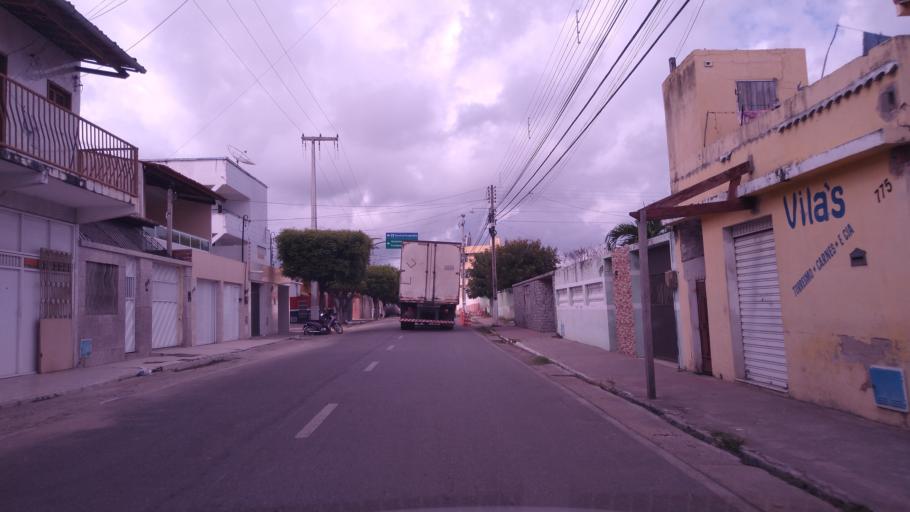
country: BR
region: Ceara
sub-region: Quixada
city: Quixada
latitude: -4.9677
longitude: -39.0196
